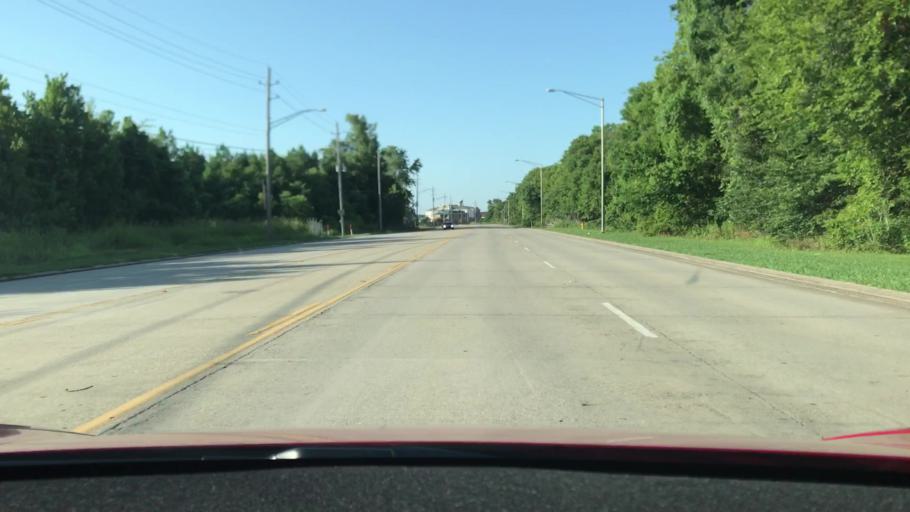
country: US
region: Louisiana
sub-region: Bossier Parish
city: Bossier City
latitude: 32.4307
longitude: -93.7257
